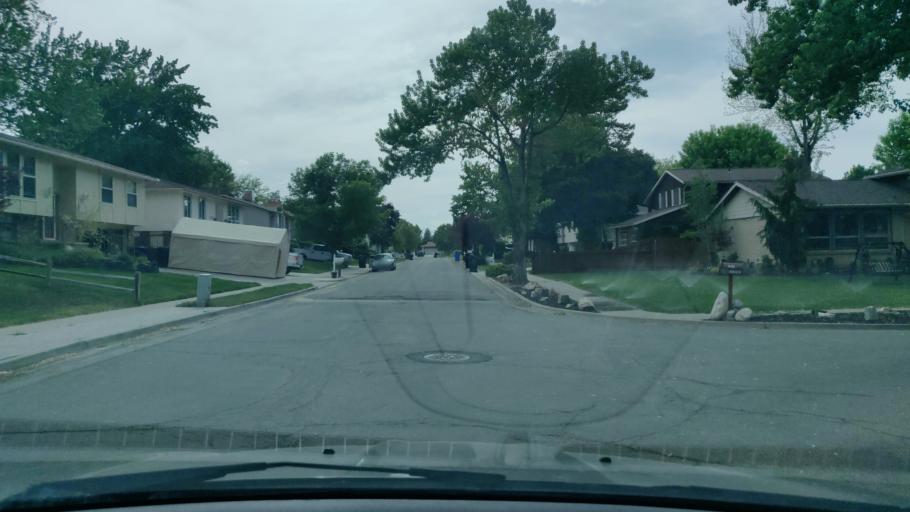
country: US
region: Utah
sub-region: Salt Lake County
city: Cottonwood Heights
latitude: 40.6200
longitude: -111.8015
